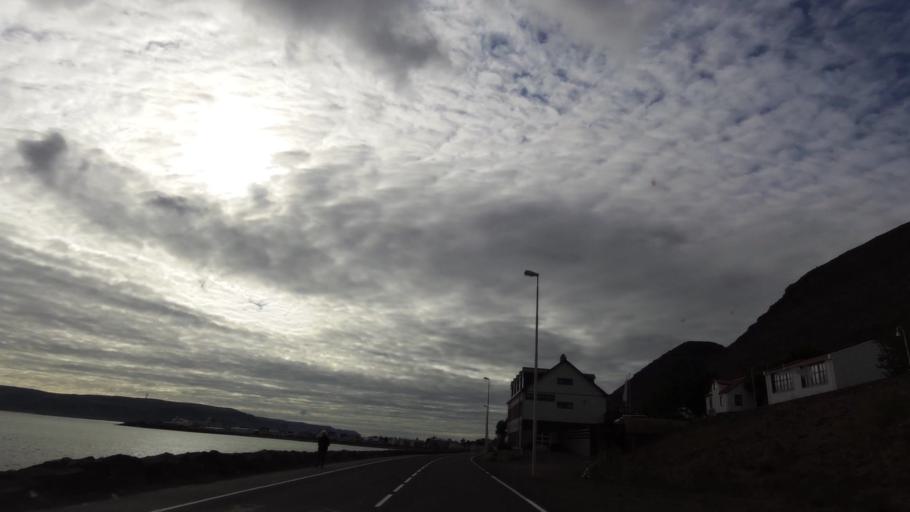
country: IS
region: West
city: Olafsvik
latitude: 65.5957
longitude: -23.9870
